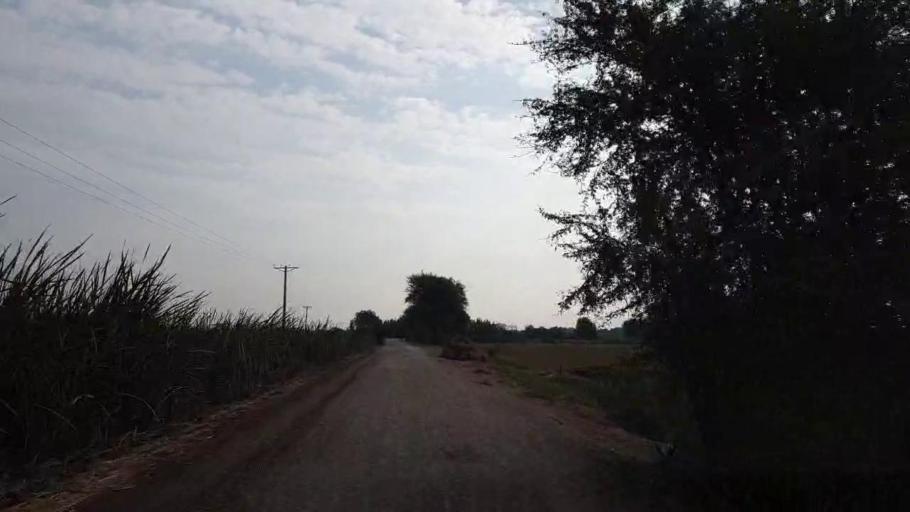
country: PK
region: Sindh
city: Tando Muhammad Khan
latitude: 25.0262
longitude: 68.4486
